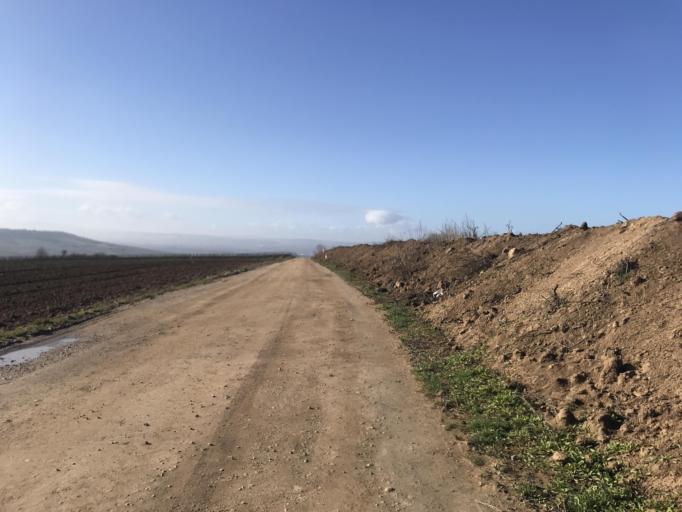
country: DE
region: Rheinland-Pfalz
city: Wolfsheim
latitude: 49.8835
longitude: 8.0280
